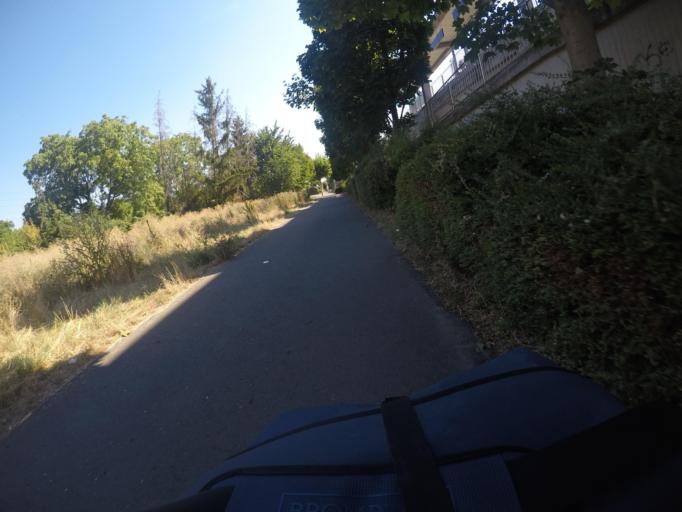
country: DE
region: Hesse
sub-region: Regierungsbezirk Darmstadt
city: Hattersheim
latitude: 50.0902
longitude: 8.5057
